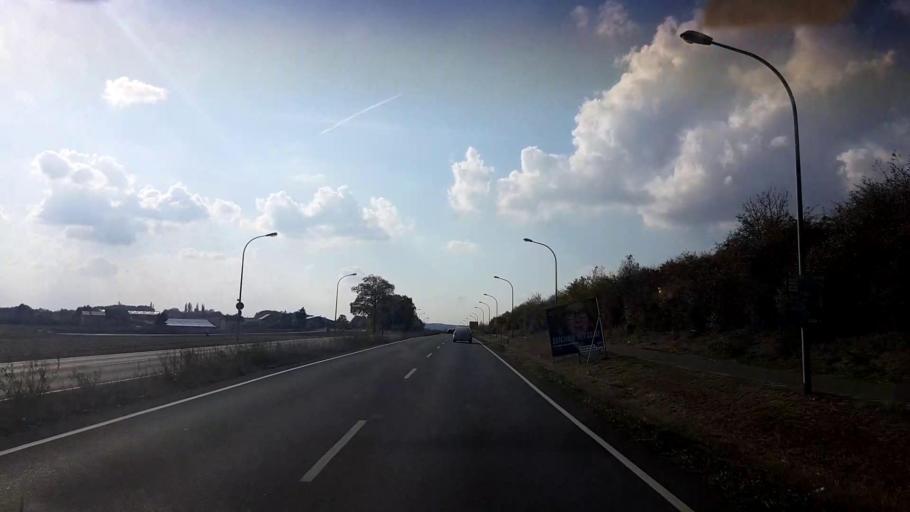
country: DE
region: Bavaria
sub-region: Upper Franconia
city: Stegaurach
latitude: 49.8714
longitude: 10.8776
